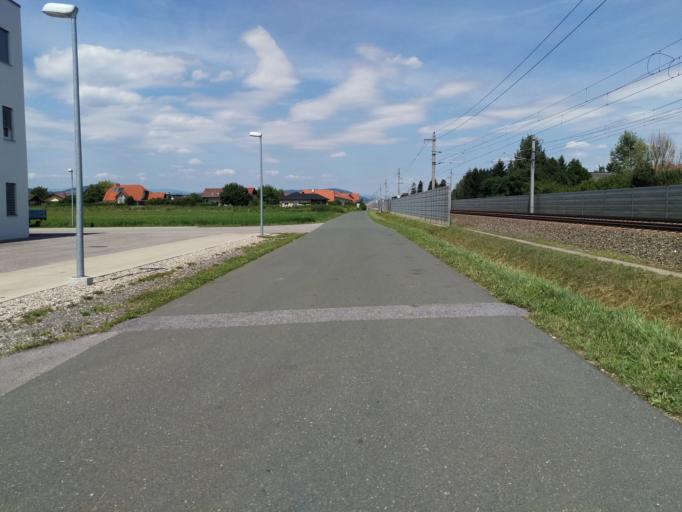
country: AT
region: Styria
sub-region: Politischer Bezirk Graz-Umgebung
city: Gossendorf
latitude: 46.9865
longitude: 15.4563
